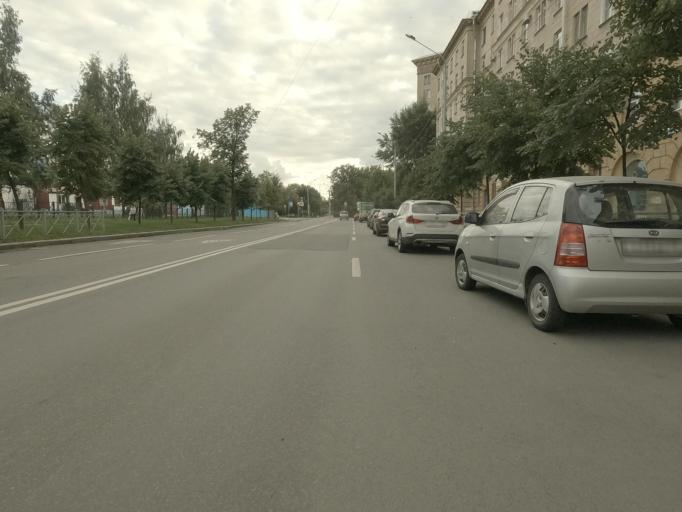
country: RU
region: St.-Petersburg
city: Avtovo
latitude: 59.8664
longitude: 30.2650
